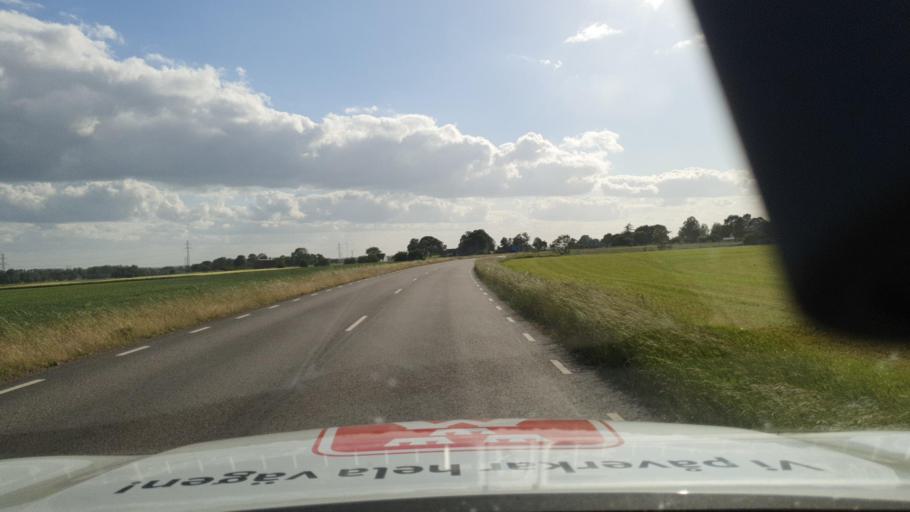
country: SE
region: Skane
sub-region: Tomelilla Kommun
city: Tomelilla
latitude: 55.5645
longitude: 13.9683
